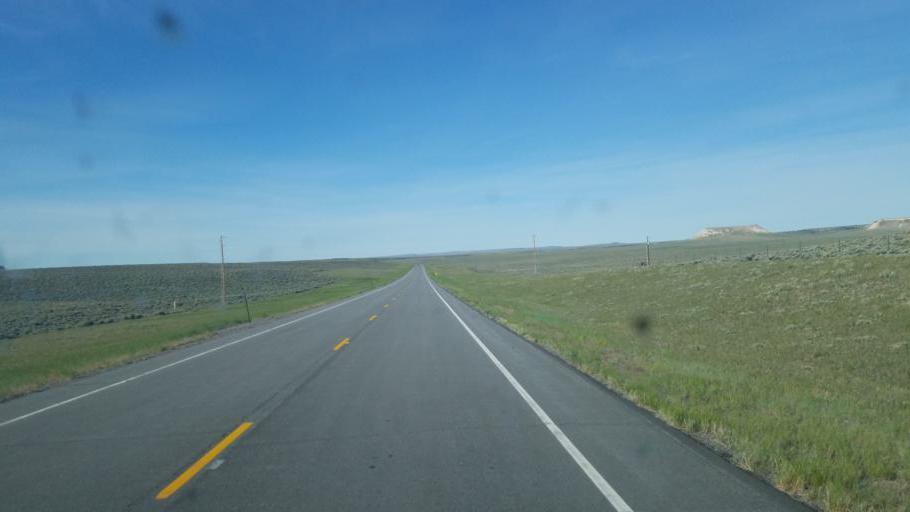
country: US
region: Wyoming
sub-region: Fremont County
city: Riverton
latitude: 42.6580
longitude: -108.1869
